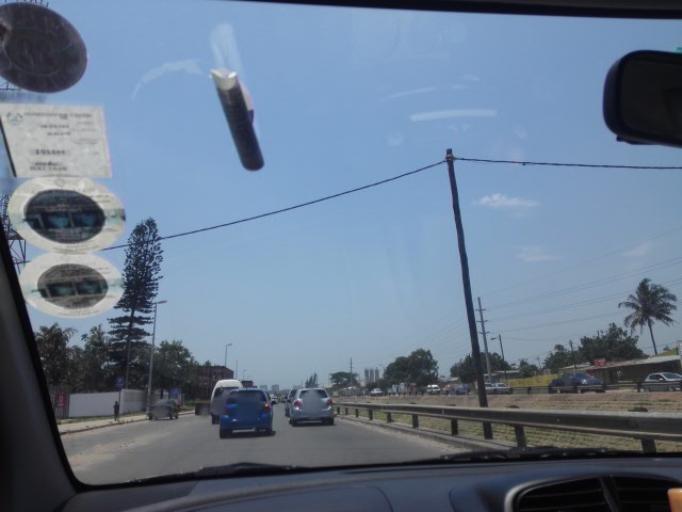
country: MZ
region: Maputo City
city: Maputo
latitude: -25.9383
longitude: 32.5678
